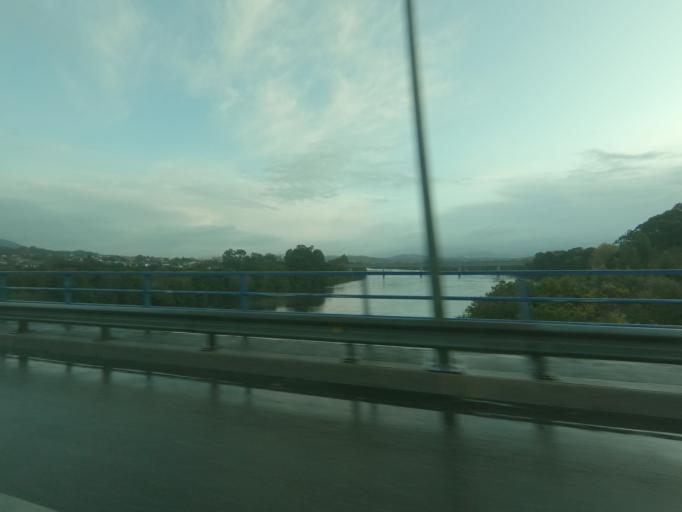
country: PT
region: Viana do Castelo
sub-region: Valenca
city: Valenca
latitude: 42.0328
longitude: -8.6532
